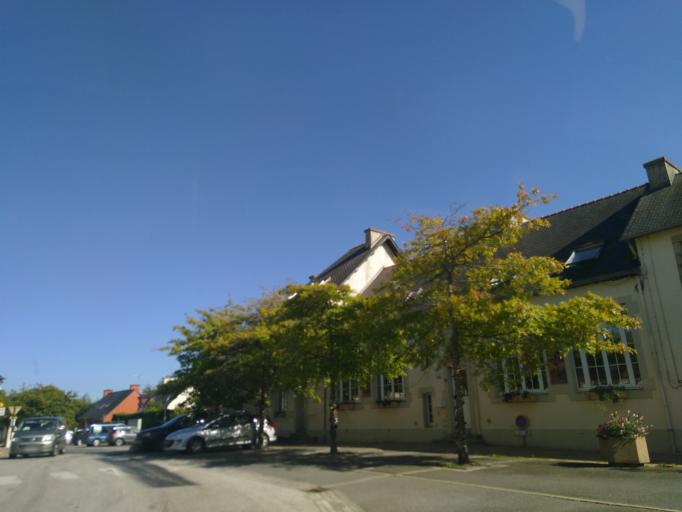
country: FR
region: Brittany
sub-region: Departement du Finistere
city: Le Faou
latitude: 48.2638
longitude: -4.1948
